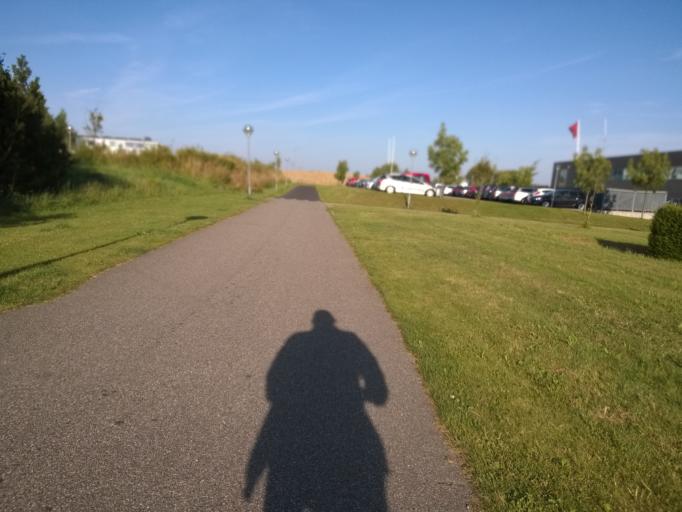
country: DK
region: Capital Region
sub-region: Egedal Kommune
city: Smorumnedre
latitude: 55.7499
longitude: 12.3005
